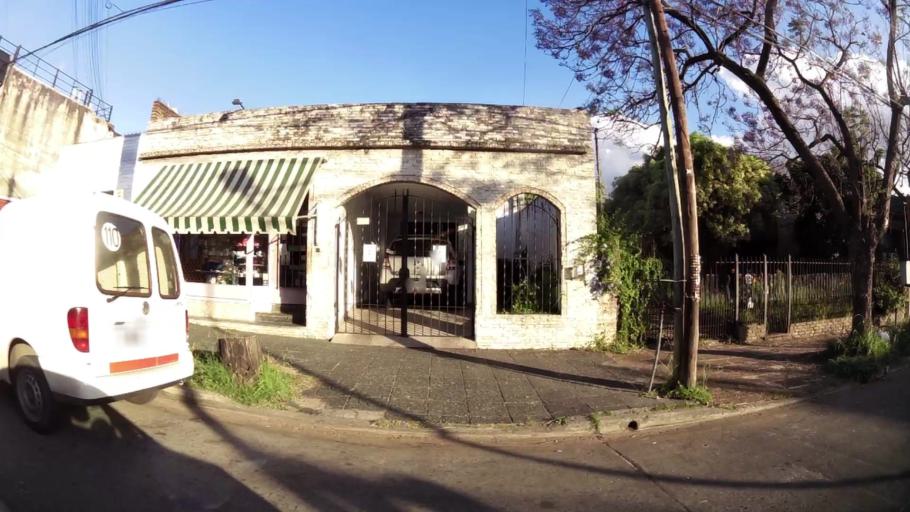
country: AR
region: Buenos Aires
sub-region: Partido de General San Martin
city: General San Martin
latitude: -34.5618
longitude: -58.5591
